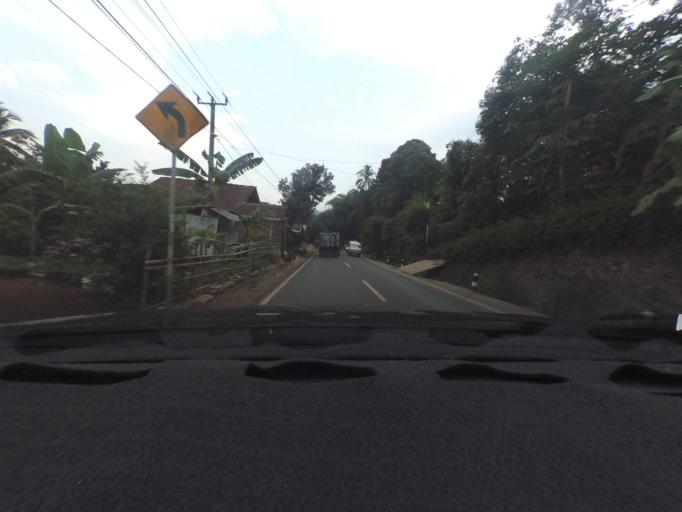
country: ID
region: West Java
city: Gunungkalong
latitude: -6.9345
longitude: 106.7734
